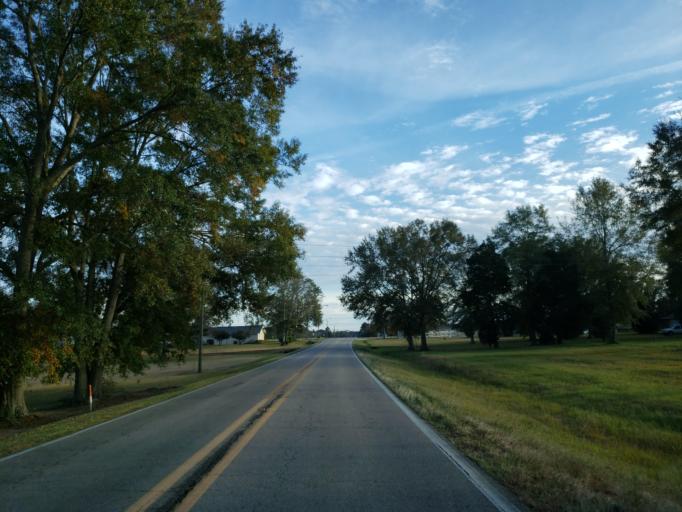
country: US
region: Mississippi
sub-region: Lamar County
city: Purvis
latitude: 31.1687
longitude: -89.4251
